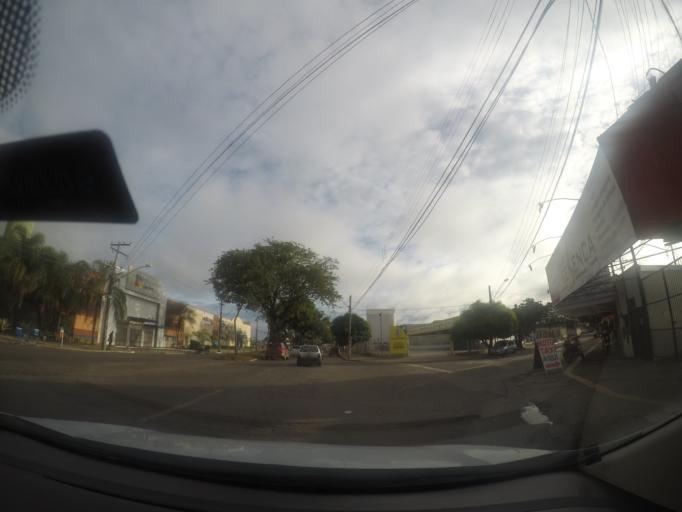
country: BR
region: Goias
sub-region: Goiania
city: Goiania
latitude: -16.6836
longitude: -49.3133
